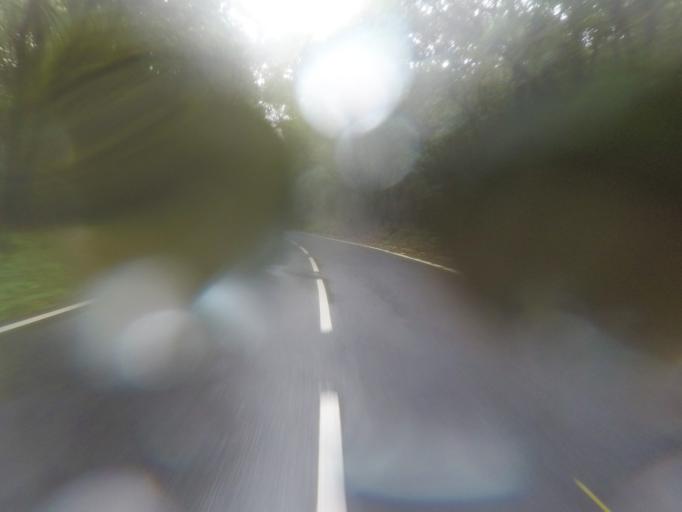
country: ES
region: Canary Islands
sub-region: Provincia de Santa Cruz de Tenerife
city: Vallehermosa
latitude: 28.1494
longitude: -17.2953
